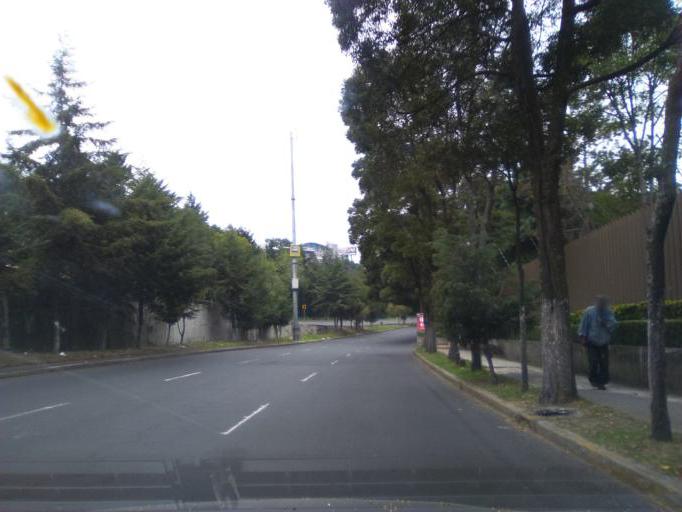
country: MX
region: Mexico City
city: Col. Bosques de las Lomas
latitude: 19.3707
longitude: -99.2653
